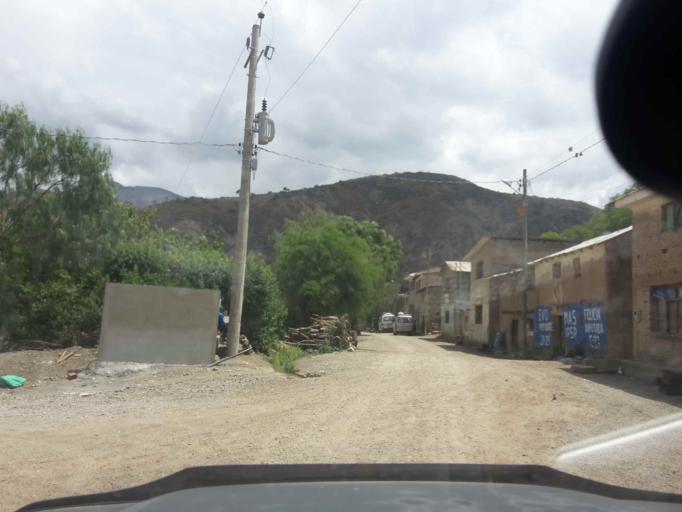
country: BO
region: Cochabamba
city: Sipe Sipe
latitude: -17.5516
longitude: -66.4719
